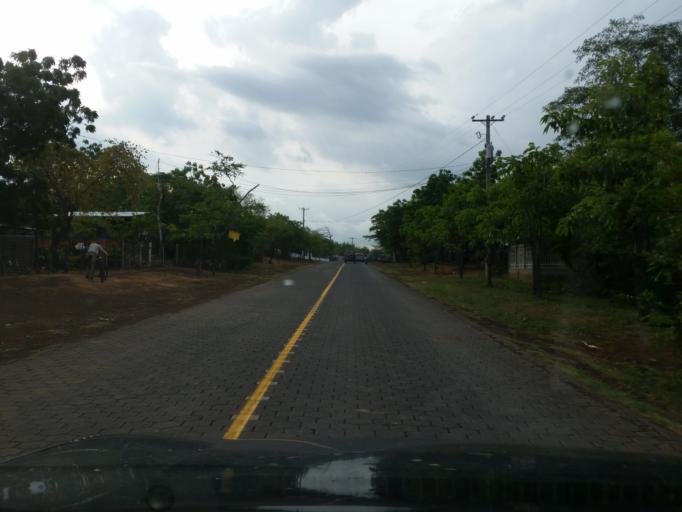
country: NI
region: Managua
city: Masachapa
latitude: 11.8320
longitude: -86.5082
